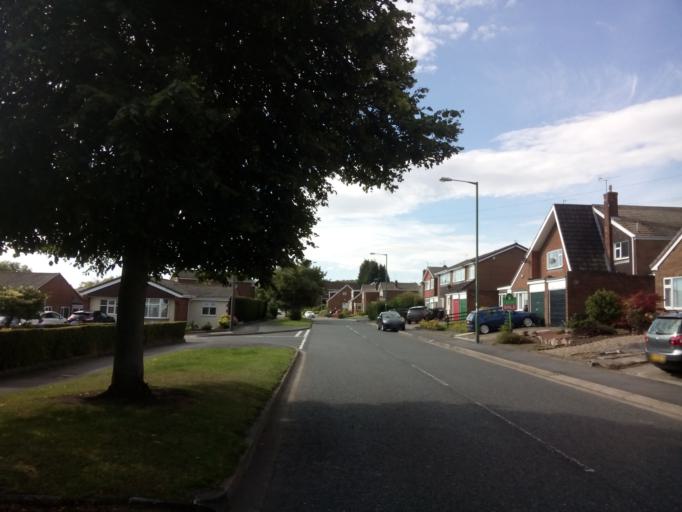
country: GB
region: England
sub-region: County Durham
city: Durham
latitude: 54.8053
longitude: -1.5676
